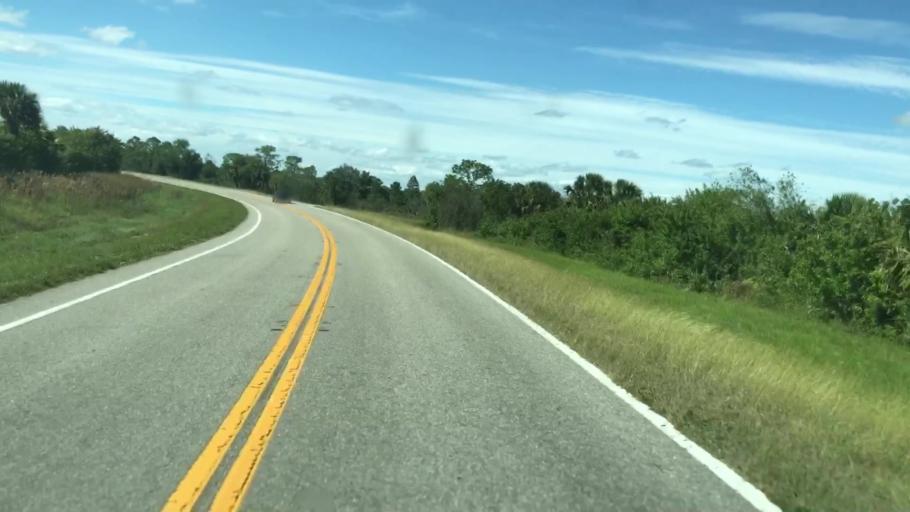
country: US
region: Florida
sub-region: Lee County
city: Olga
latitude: 26.7391
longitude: -81.7144
